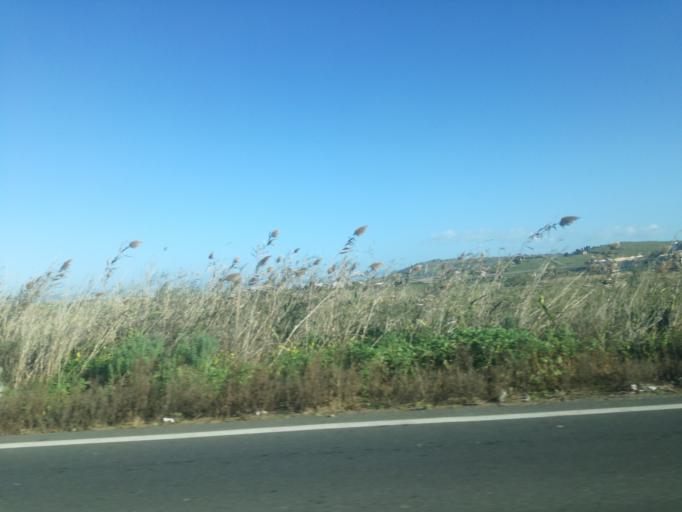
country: IT
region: Sicily
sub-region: Provincia di Caltanissetta
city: Gela
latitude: 37.0526
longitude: 14.3090
